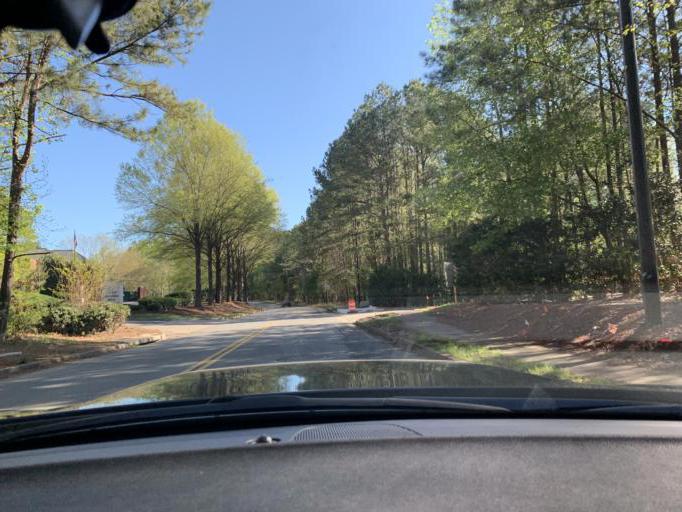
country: US
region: Georgia
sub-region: Fulton County
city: Alpharetta
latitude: 34.0872
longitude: -84.2534
